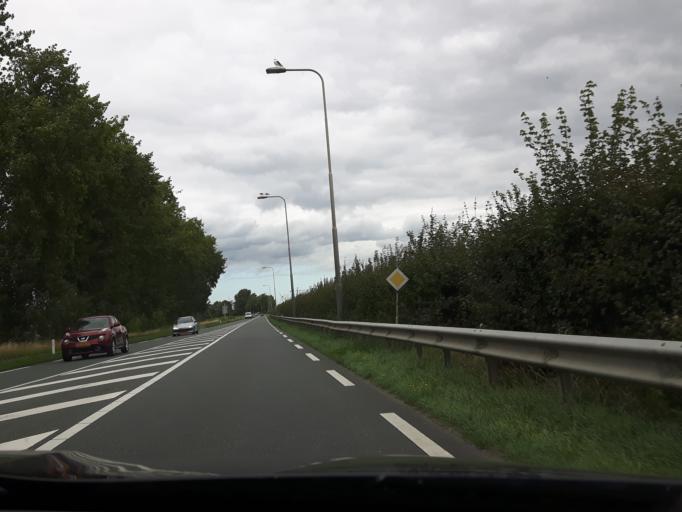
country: NL
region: Zeeland
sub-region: Gemeente Terneuzen
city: Sluiskil
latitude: 51.2614
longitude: 3.8291
